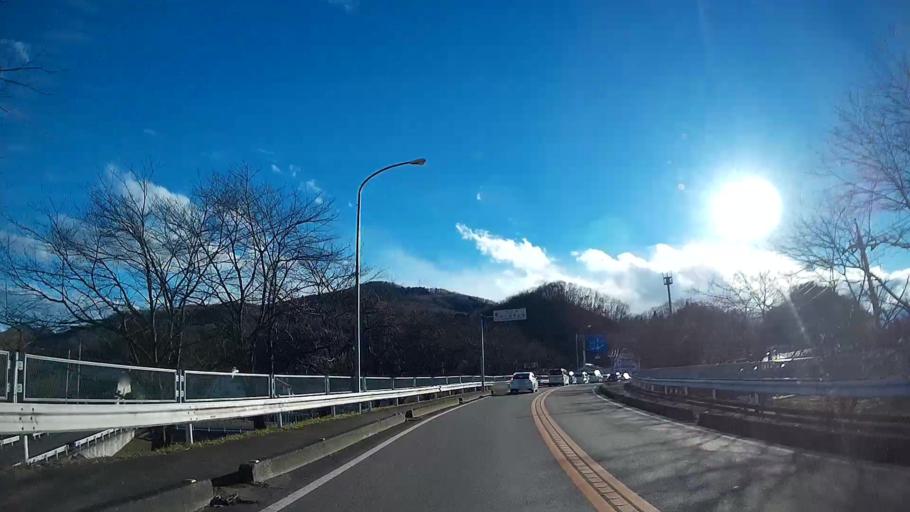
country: JP
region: Saitama
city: Yorii
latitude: 36.0790
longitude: 139.1106
